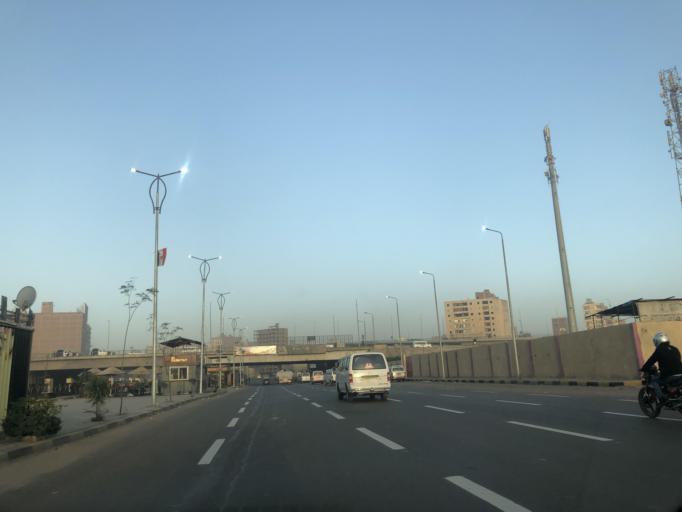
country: EG
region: Al Jizah
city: Al Jizah
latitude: 29.9739
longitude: 31.1744
